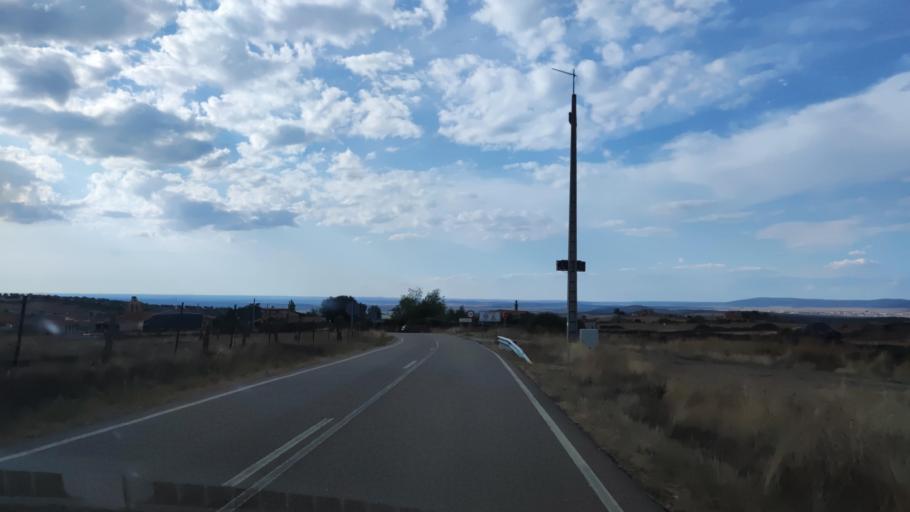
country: ES
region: Castille and Leon
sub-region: Provincia de Salamanca
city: Pastores
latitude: 40.5138
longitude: -6.5066
